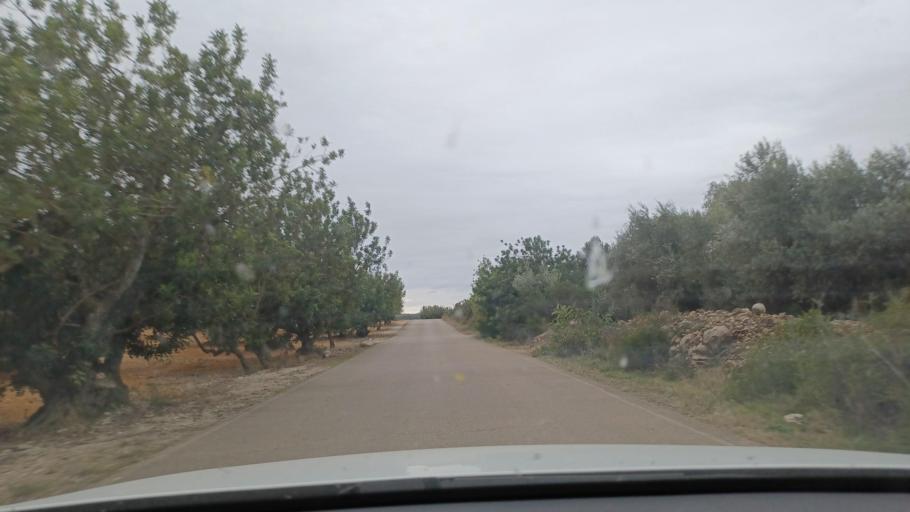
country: ES
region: Valencia
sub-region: Provincia de Castello
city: Canet lo Roig
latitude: 40.5729
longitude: 0.2778
